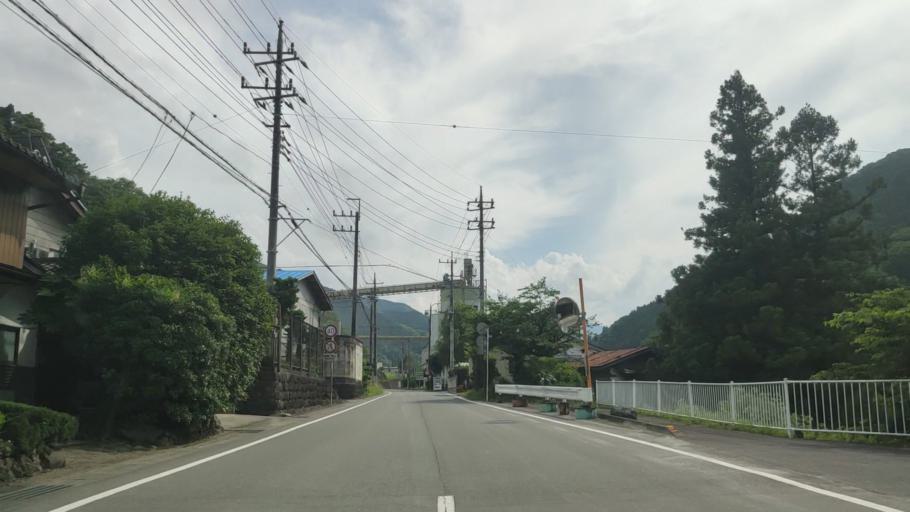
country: JP
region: Gunma
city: Tomioka
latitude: 36.1879
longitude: 138.7497
